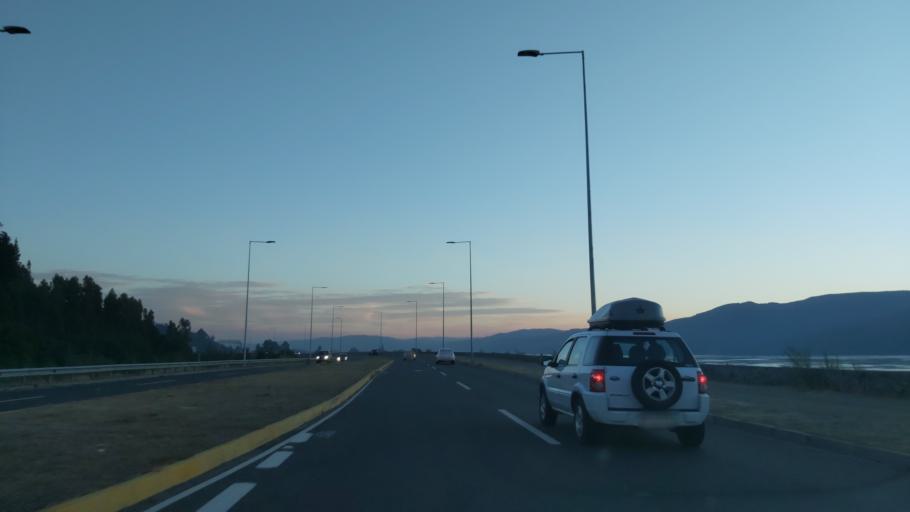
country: CL
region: Biobio
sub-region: Provincia de Concepcion
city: Concepcion
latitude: -36.8694
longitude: -73.0440
